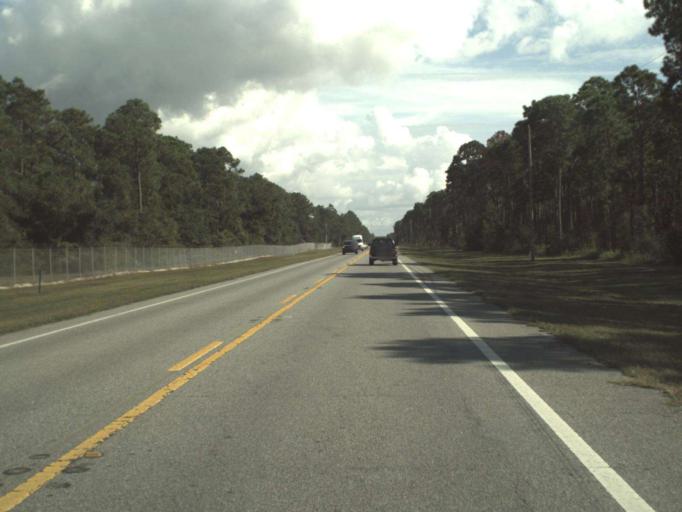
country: US
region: Florida
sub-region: Bay County
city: Tyndall Air Force Base
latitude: 30.0537
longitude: -85.5691
